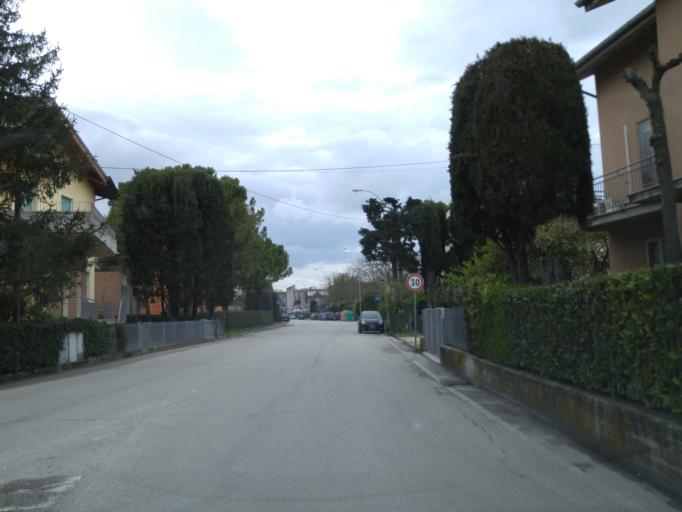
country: IT
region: The Marches
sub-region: Provincia di Pesaro e Urbino
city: Fano
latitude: 43.8320
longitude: 13.0065
